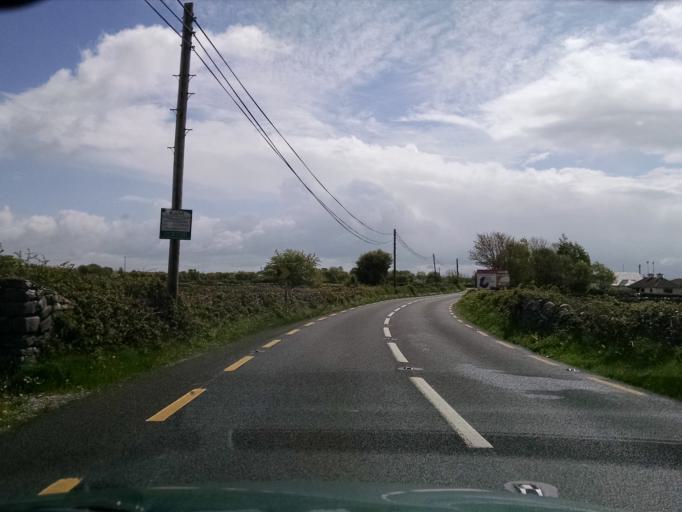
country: IE
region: Connaught
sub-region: County Galway
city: Oranmore
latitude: 53.1411
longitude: -8.9668
